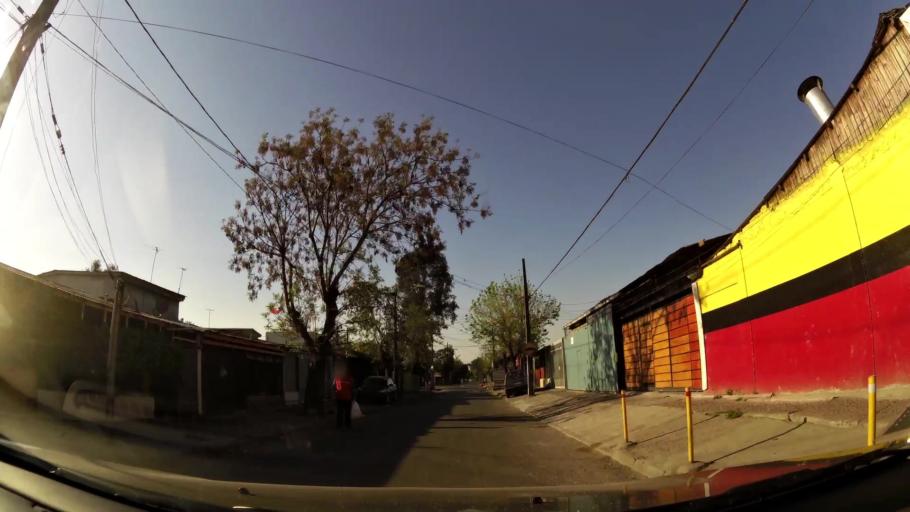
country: CL
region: Santiago Metropolitan
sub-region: Provincia de Santiago
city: La Pintana
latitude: -33.5825
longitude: -70.6602
